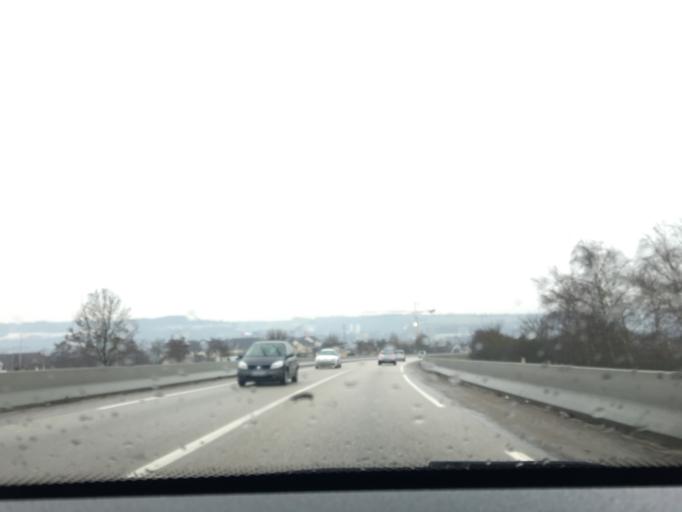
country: FR
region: Ile-de-France
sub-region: Departement des Yvelines
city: Limay
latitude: 48.9900
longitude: 1.7477
